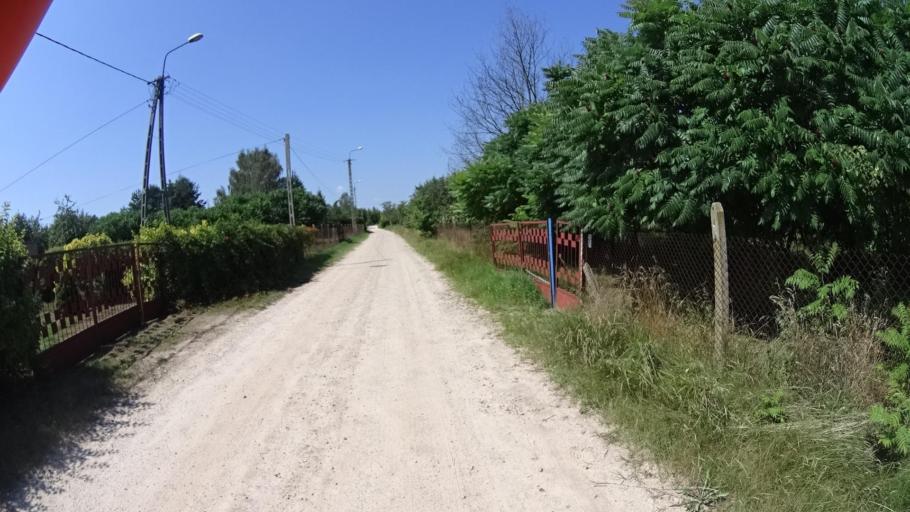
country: PL
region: Masovian Voivodeship
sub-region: Powiat piaseczynski
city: Tarczyn
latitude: 51.9764
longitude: 20.8572
